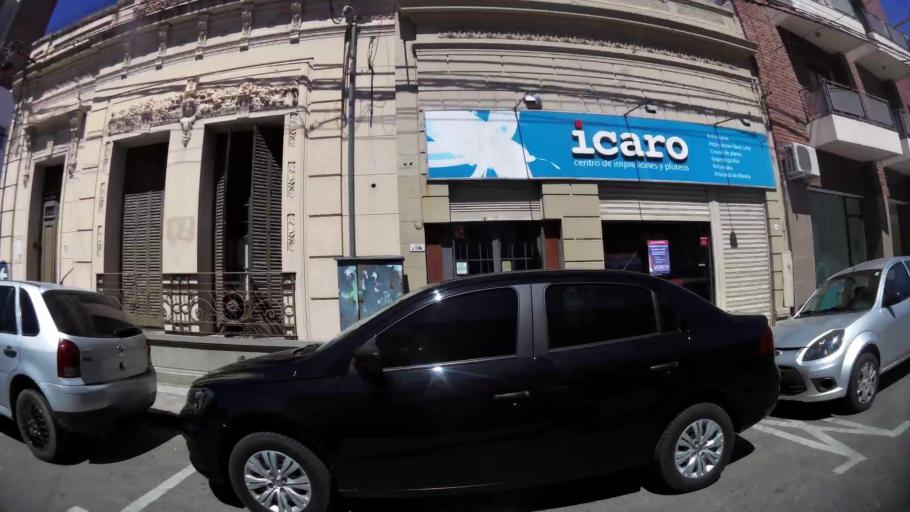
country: AR
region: Santa Fe
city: Santa Fe de la Vera Cruz
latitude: -31.6551
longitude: -60.7078
